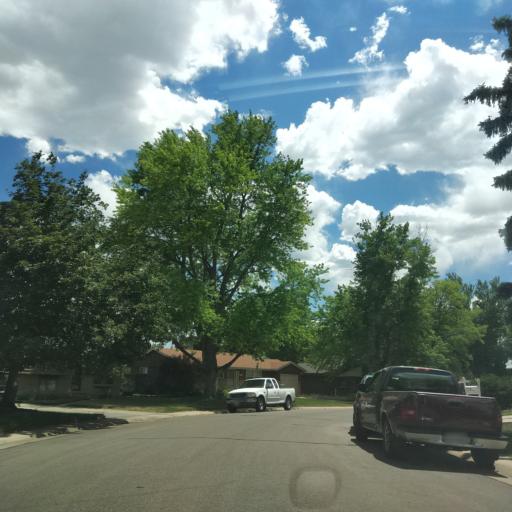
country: US
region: Colorado
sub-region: Jefferson County
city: Lakewood
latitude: 39.6849
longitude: -105.0947
